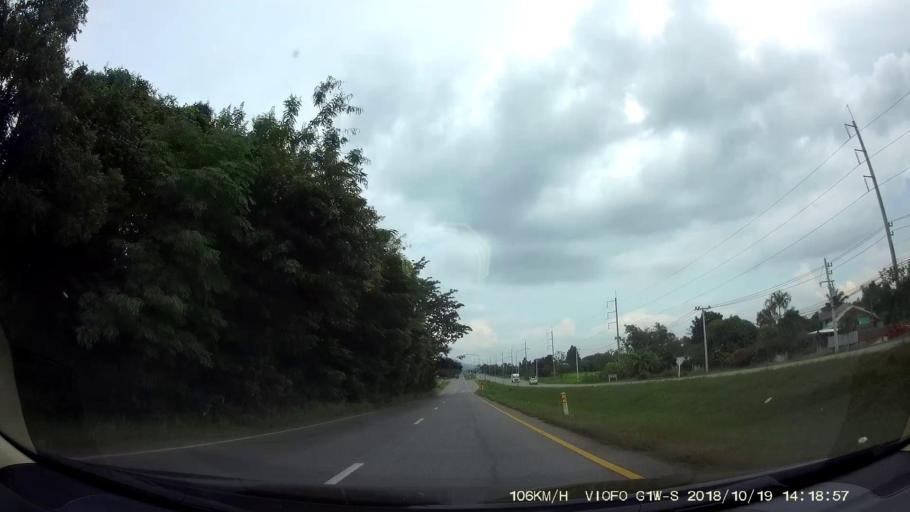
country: TH
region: Chaiyaphum
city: Kaeng Khro
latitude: 16.0219
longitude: 102.2404
